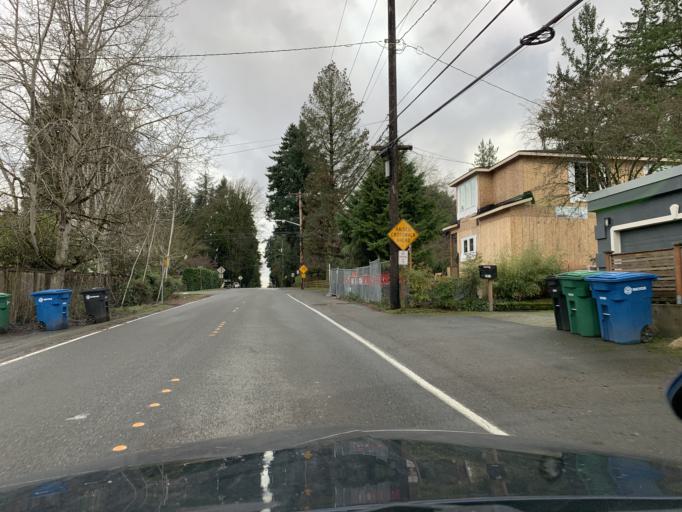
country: US
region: Washington
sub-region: King County
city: Mercer Island
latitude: 47.5849
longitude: -122.2432
